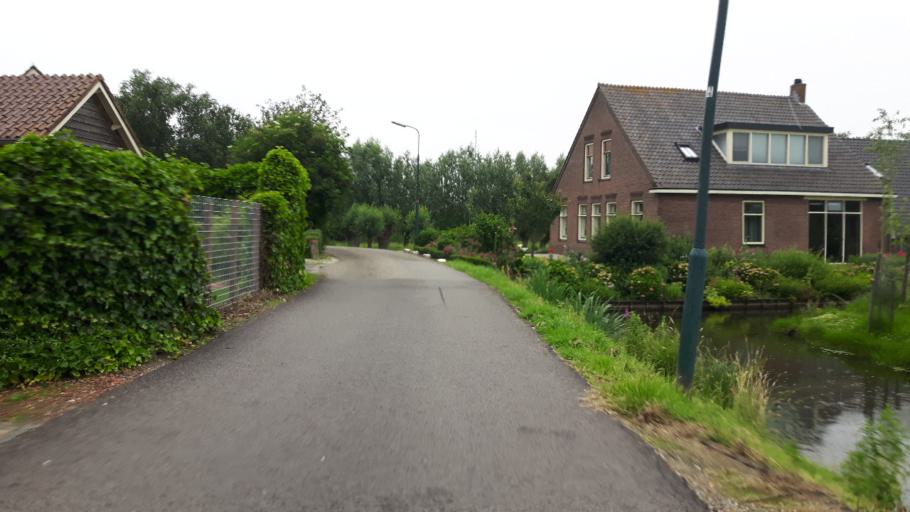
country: NL
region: Utrecht
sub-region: Gemeente Lopik
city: Lopik
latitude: 51.9672
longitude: 4.9025
